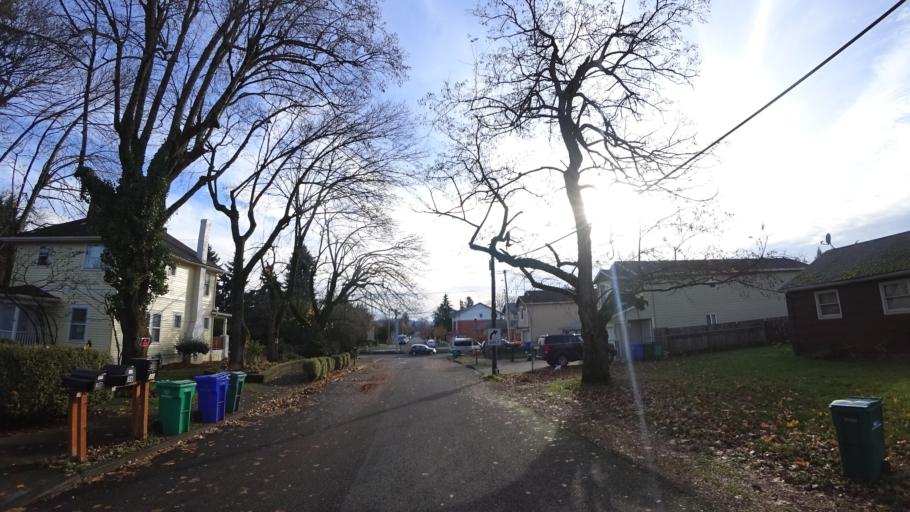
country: US
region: Oregon
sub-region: Multnomah County
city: Lents
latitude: 45.5229
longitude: -122.5158
